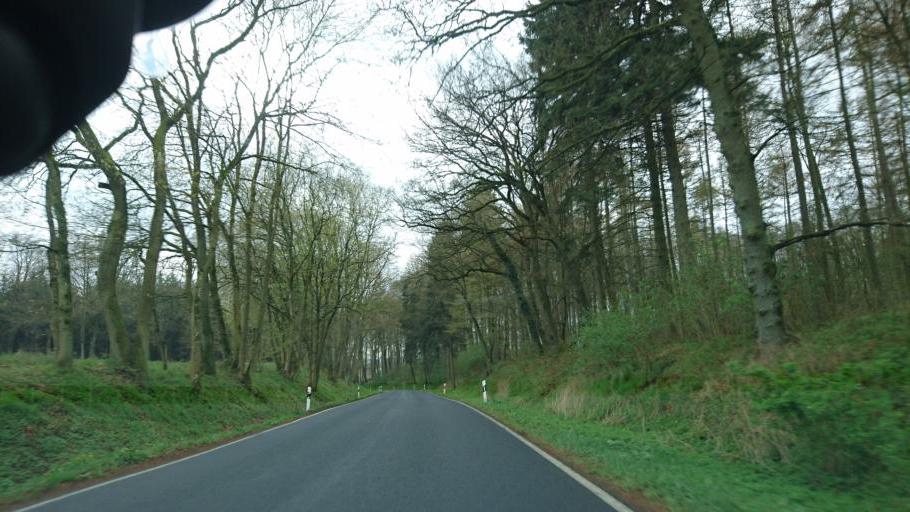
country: DE
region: Mecklenburg-Vorpommern
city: Bad Sulze
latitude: 54.1302
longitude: 12.6947
